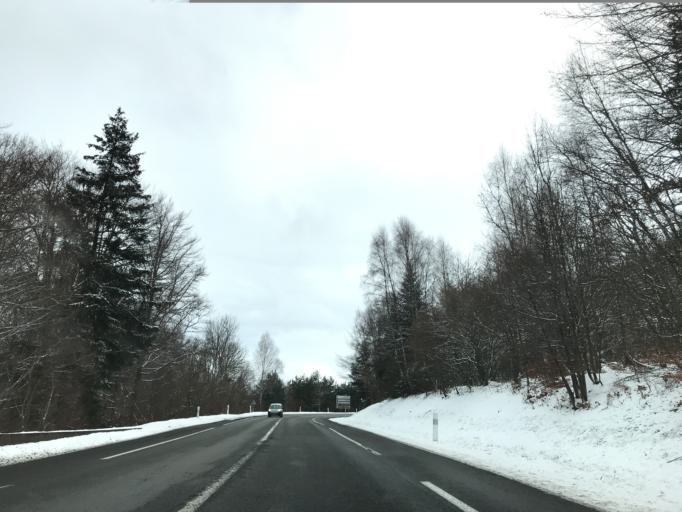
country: FR
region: Auvergne
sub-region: Departement du Puy-de-Dome
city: Aydat
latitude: 45.6848
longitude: 2.9684
